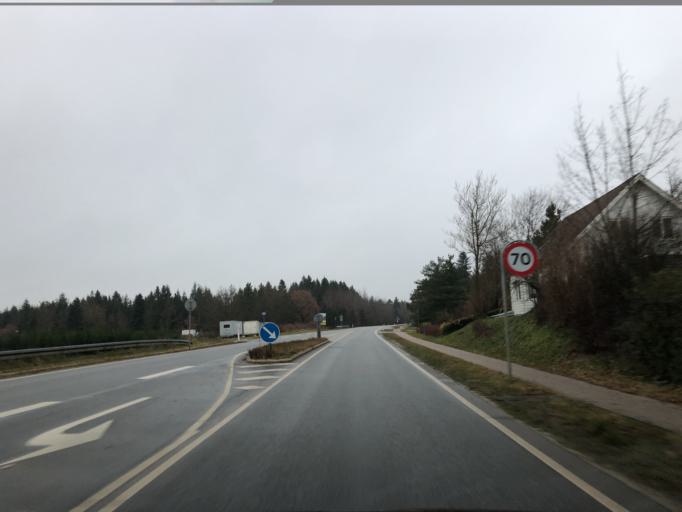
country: DK
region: Central Jutland
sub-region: Herning Kommune
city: Lind
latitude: 56.0832
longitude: 8.9822
